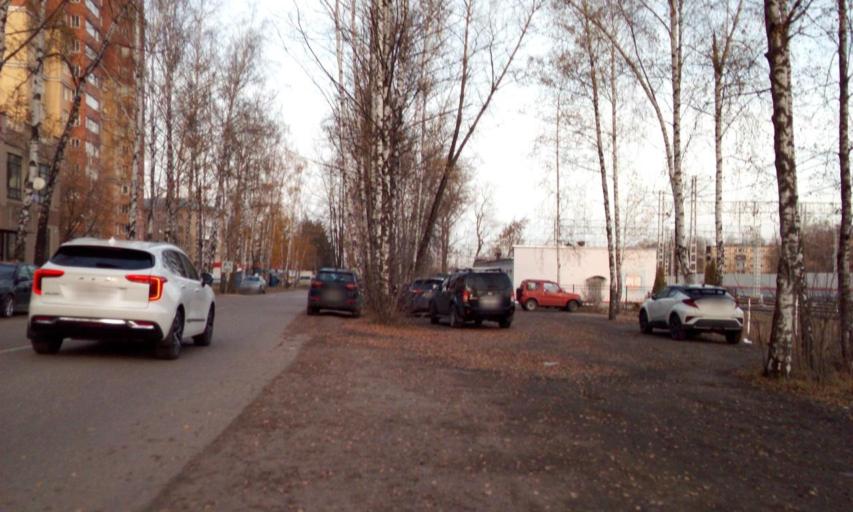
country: RU
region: Moskovskaya
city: Aprelevka
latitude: 55.5526
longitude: 37.0712
